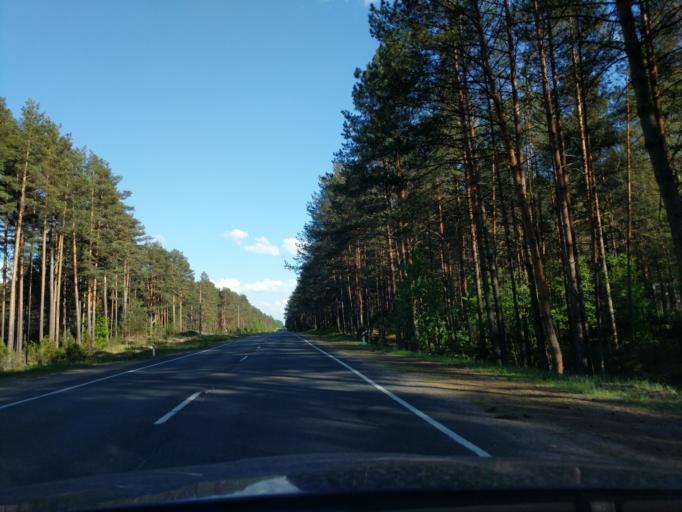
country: BY
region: Minsk
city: Myadzyel
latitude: 54.8230
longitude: 26.9531
